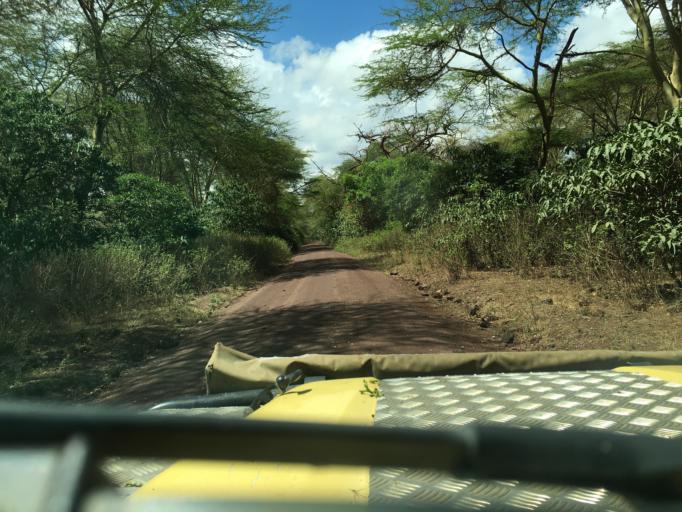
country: TZ
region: Arusha
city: Mto wa Mbu
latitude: -3.4066
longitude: 35.8245
